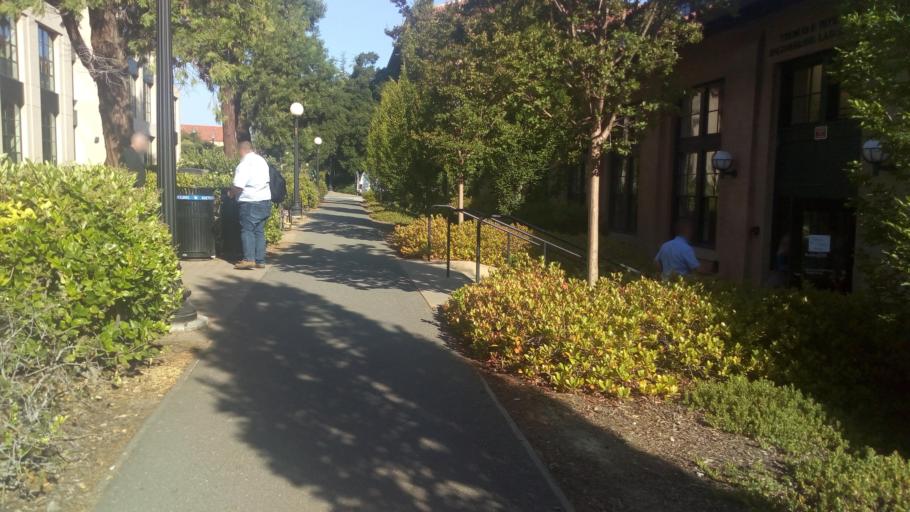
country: US
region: California
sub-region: Santa Clara County
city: Stanford
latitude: 37.4260
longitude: -122.1717
